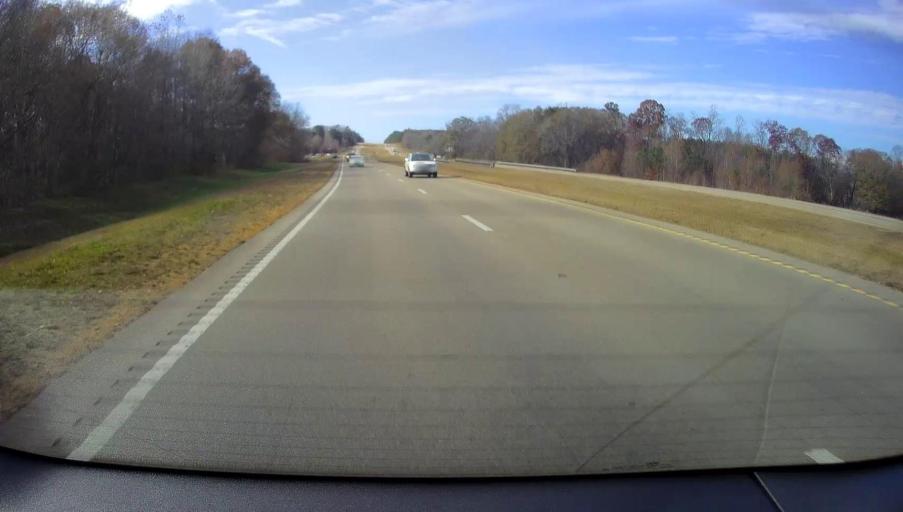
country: US
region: Mississippi
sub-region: Alcorn County
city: Farmington
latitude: 34.8507
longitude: -88.3422
